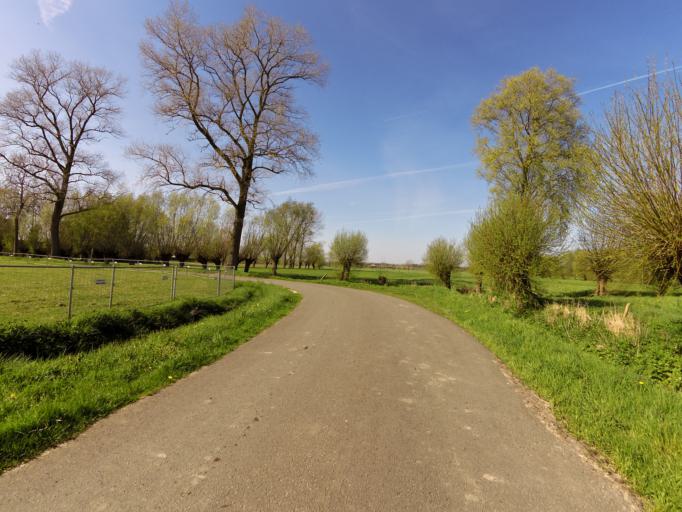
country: BE
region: Flanders
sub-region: Provincie West-Vlaanderen
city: Jabbeke
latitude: 51.1834
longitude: 3.0761
